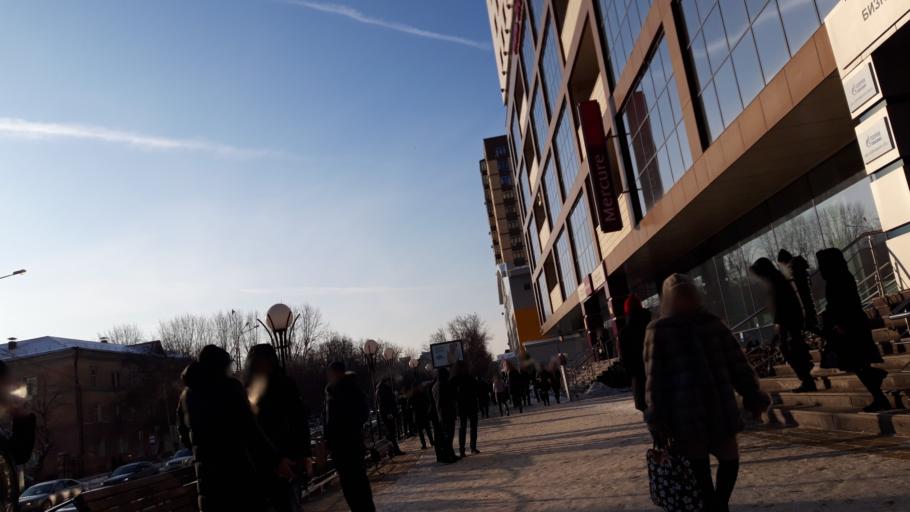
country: RU
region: Tjumen
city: Tyumen
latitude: 57.1521
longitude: 65.5675
